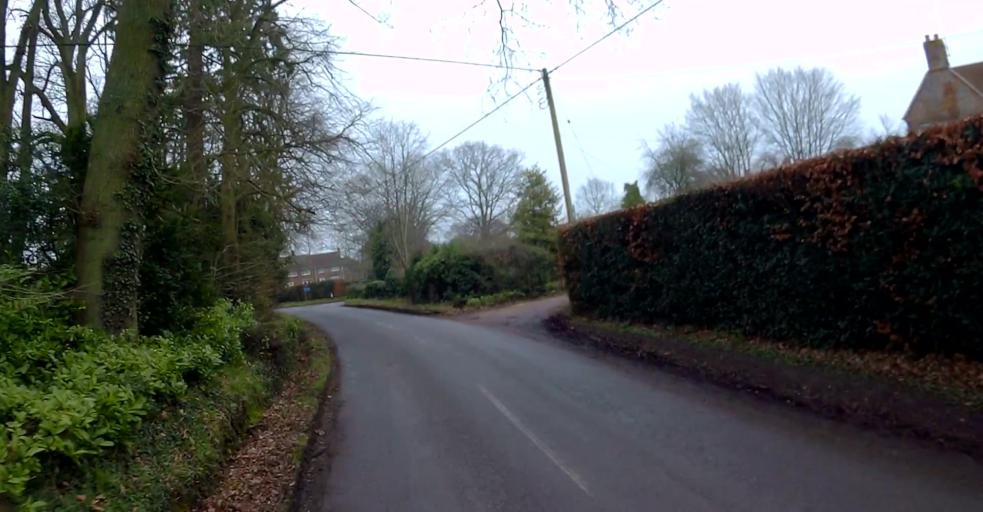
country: GB
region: England
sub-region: Hampshire
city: Hook
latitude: 51.2998
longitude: -0.9828
